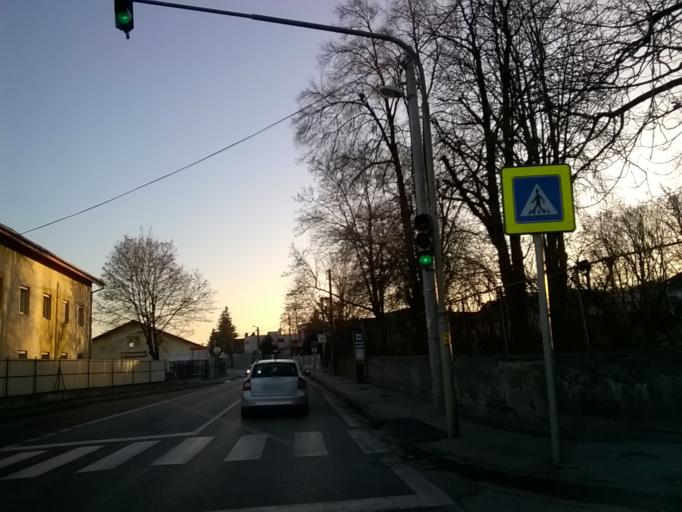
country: SK
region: Nitriansky
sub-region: Okres Nitra
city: Nitra
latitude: 48.2937
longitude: 18.0710
